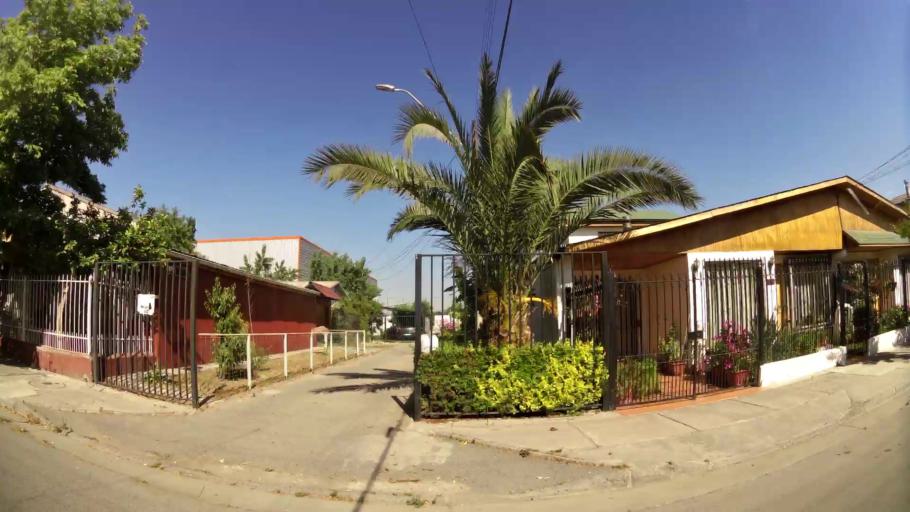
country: CL
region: Santiago Metropolitan
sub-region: Provincia de Maipo
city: San Bernardo
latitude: -33.5577
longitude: -70.7085
